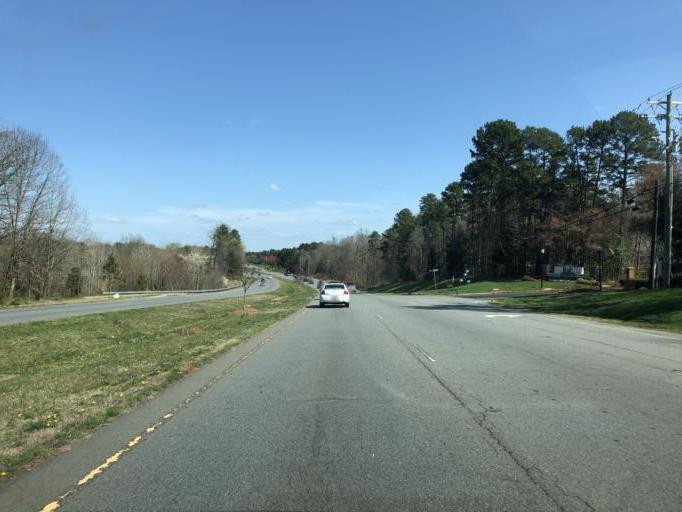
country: US
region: North Carolina
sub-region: Mecklenburg County
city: Huntersville
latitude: 35.3329
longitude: -80.8146
